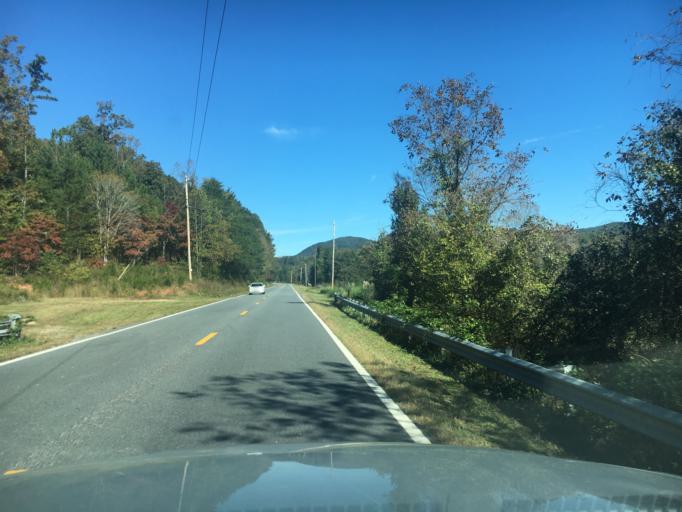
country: US
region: North Carolina
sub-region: Rutherford County
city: Spindale
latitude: 35.5125
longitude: -81.8556
